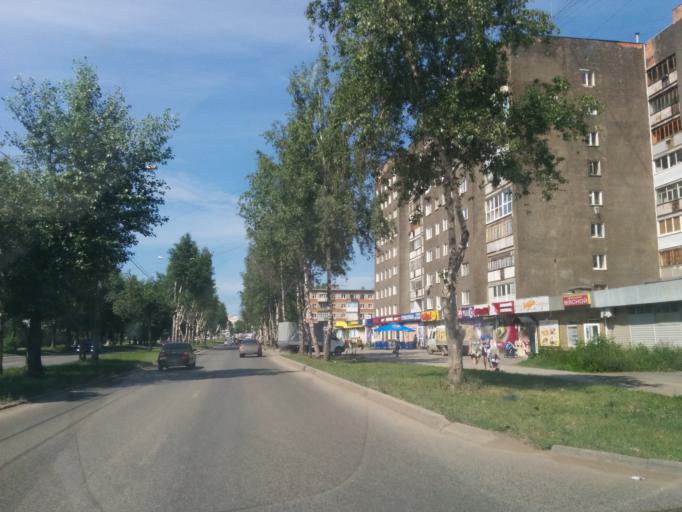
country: RU
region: Perm
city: Perm
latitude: 58.0124
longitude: 56.2939
